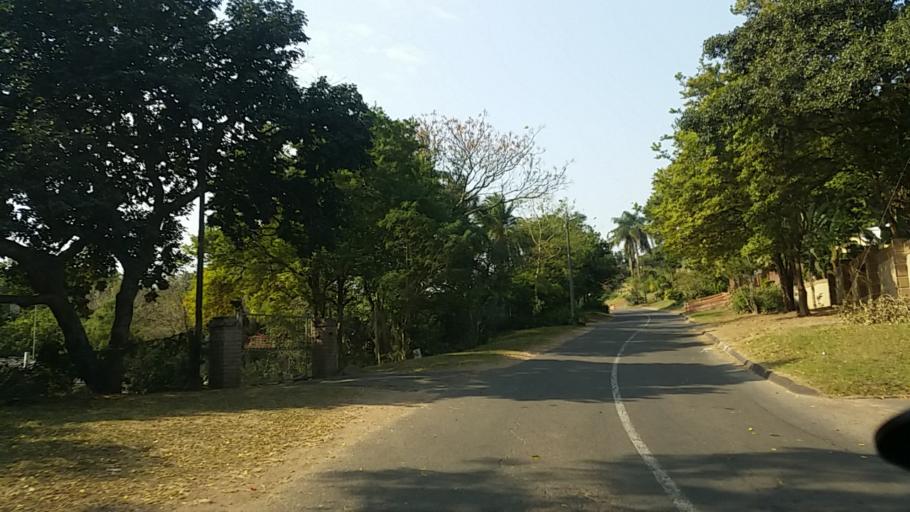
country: ZA
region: KwaZulu-Natal
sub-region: eThekwini Metropolitan Municipality
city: Berea
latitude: -29.8449
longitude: 30.9431
